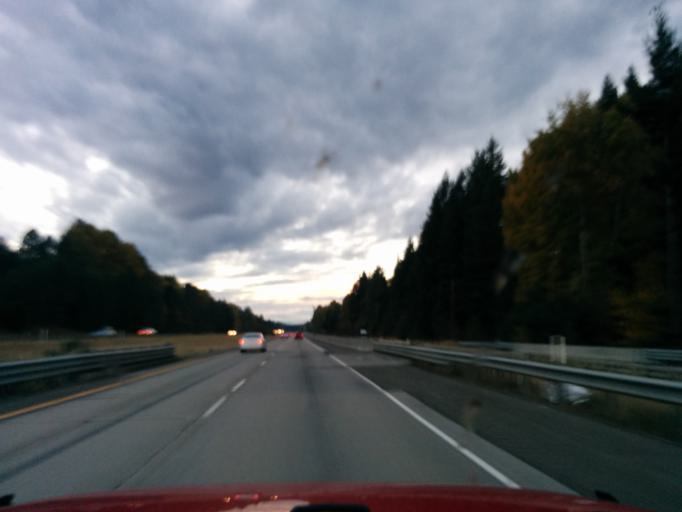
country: US
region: Washington
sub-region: Kittitas County
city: Cle Elum
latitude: 47.2041
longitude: -121.0798
